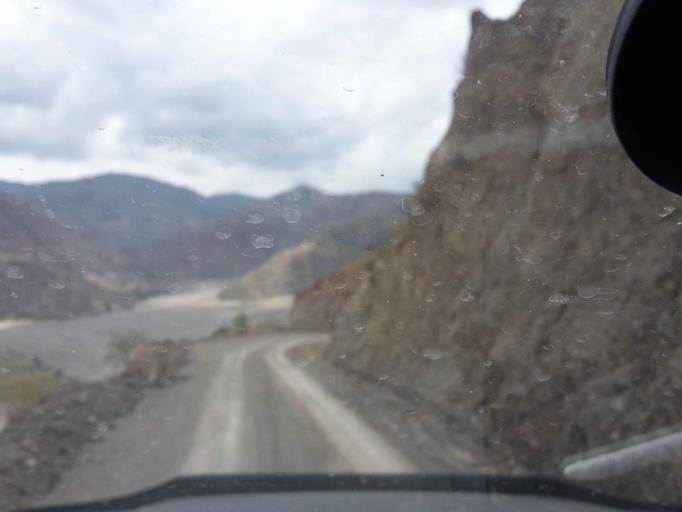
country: BO
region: Cochabamba
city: Colchani
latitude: -17.5156
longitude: -66.6066
